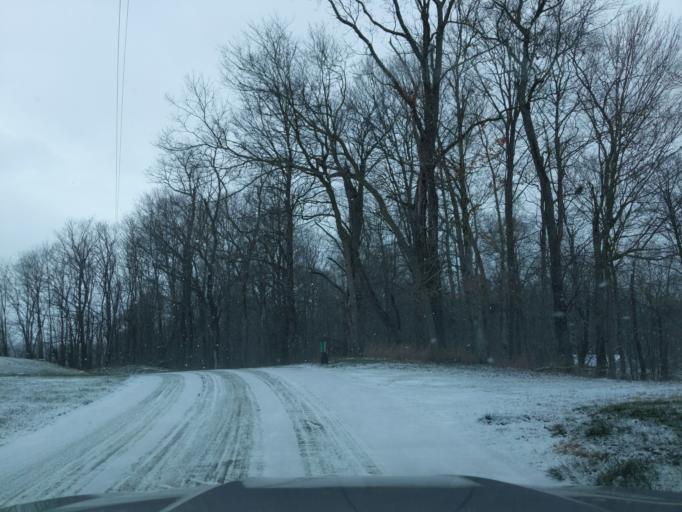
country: US
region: Indiana
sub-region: Decatur County
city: Westport
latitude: 39.2293
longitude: -85.5124
